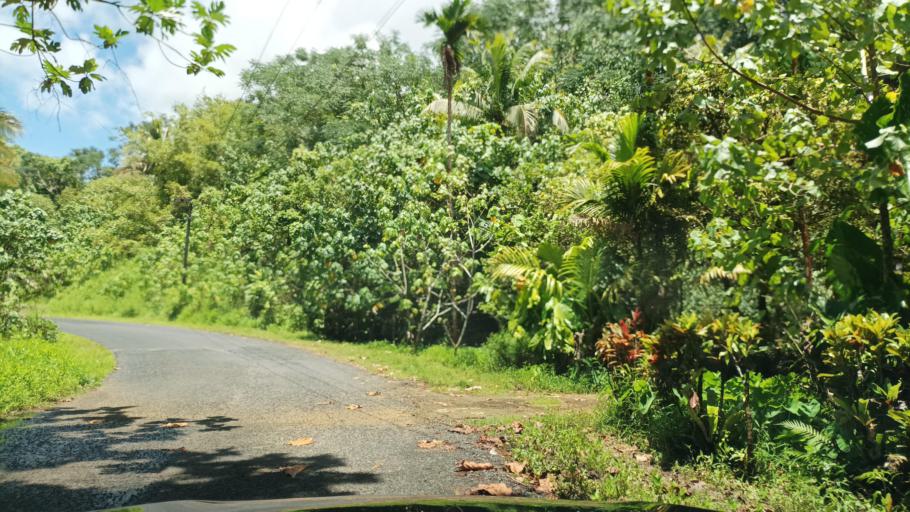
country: FM
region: Pohnpei
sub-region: Madolenihm Municipality
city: Madolenihm Municipality Government
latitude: 6.8587
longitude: 158.2915
